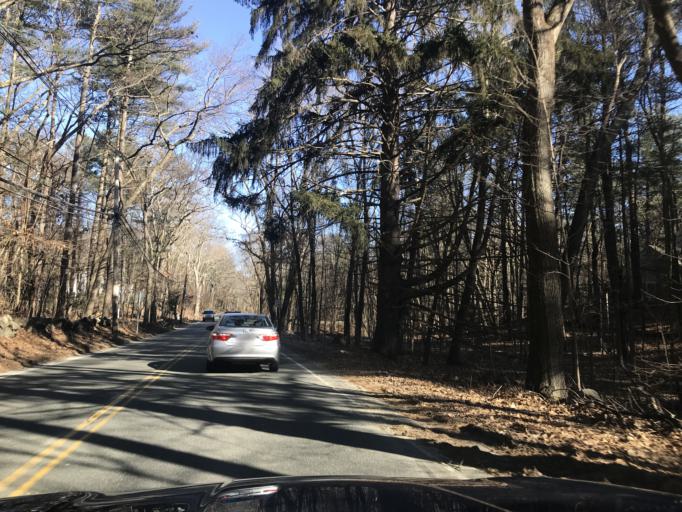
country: US
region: Massachusetts
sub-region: Essex County
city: Groveland
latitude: 42.7102
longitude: -71.0576
